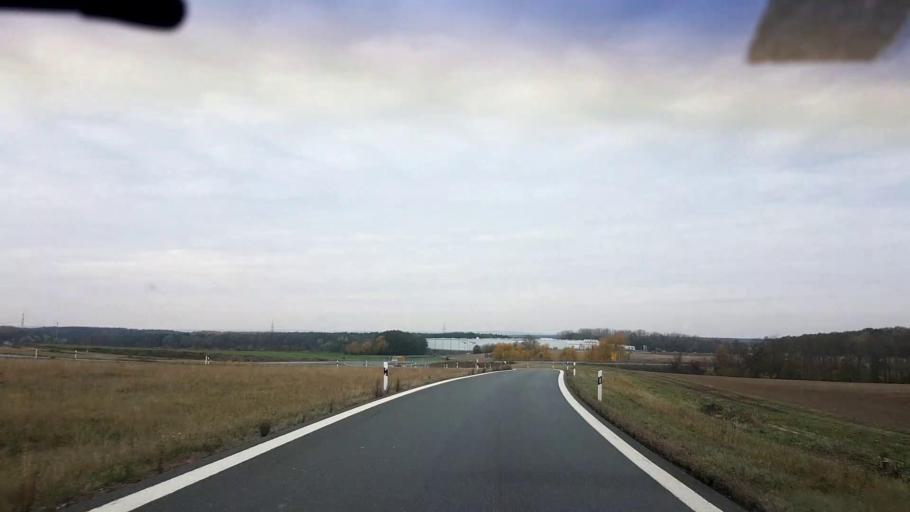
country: DE
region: Bavaria
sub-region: Regierungsbezirk Unterfranken
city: Wiesentheid
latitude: 49.7756
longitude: 10.3504
